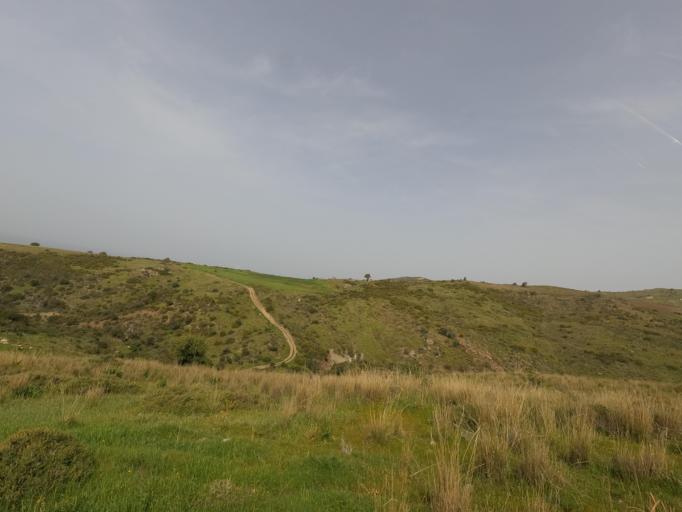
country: CY
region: Pafos
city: Pegeia
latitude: 34.9555
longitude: 32.3383
